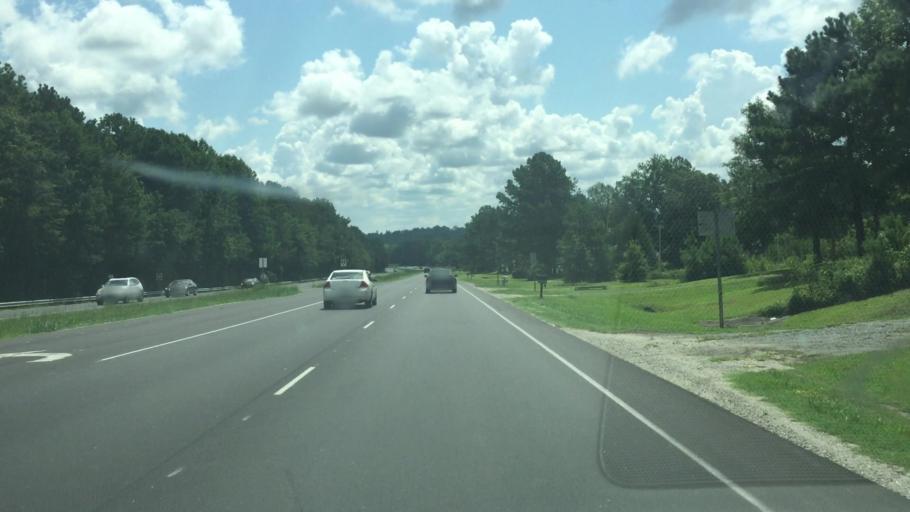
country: US
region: North Carolina
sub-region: Richmond County
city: Cordova
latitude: 34.9462
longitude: -79.8952
